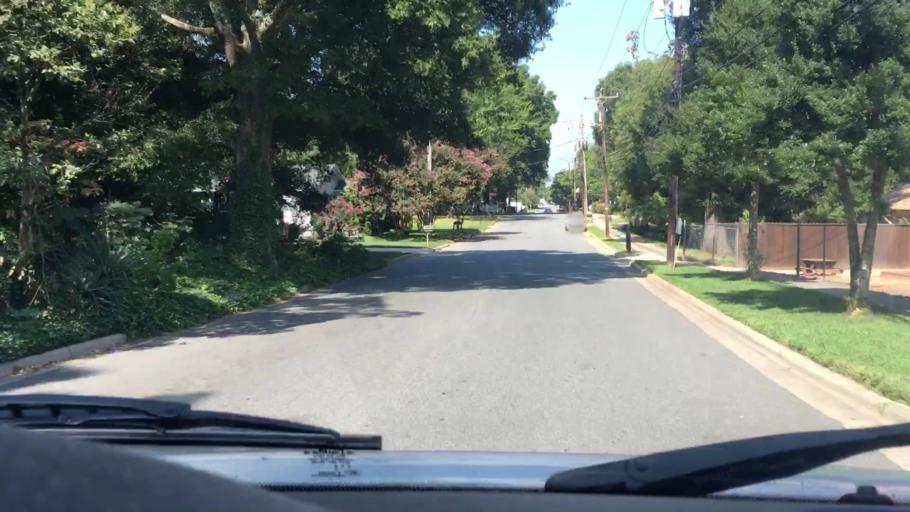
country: US
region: North Carolina
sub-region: Mecklenburg County
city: Cornelius
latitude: 35.4977
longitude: -80.8544
